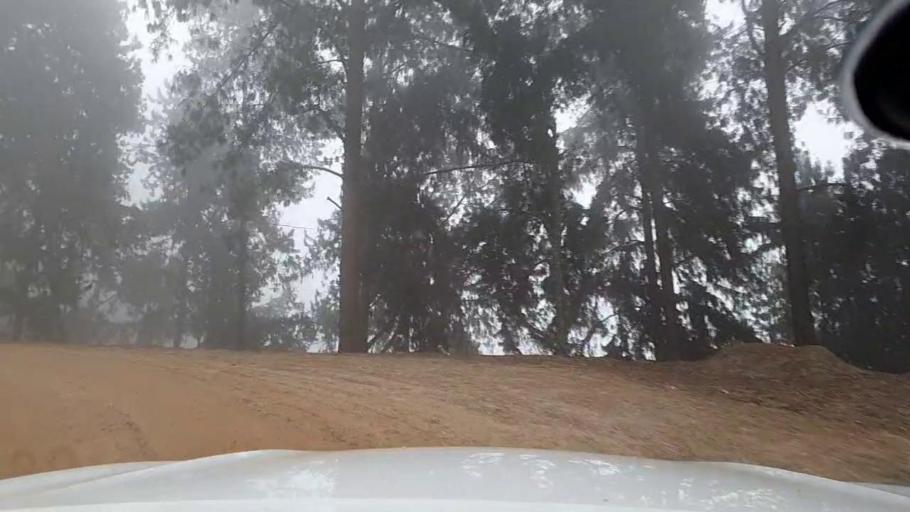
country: BI
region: Cibitoke
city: Cibitoke
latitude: -2.5981
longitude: 29.1953
